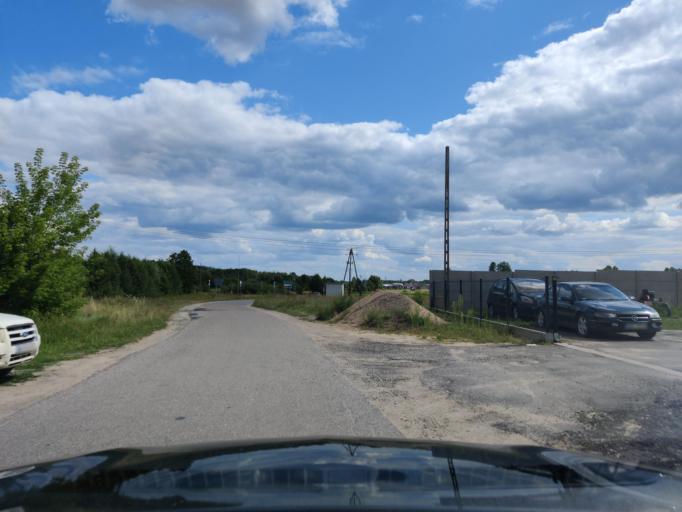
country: PL
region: Masovian Voivodeship
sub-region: Powiat sokolowski
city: Kosow Lacki
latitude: 52.5820
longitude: 22.1442
